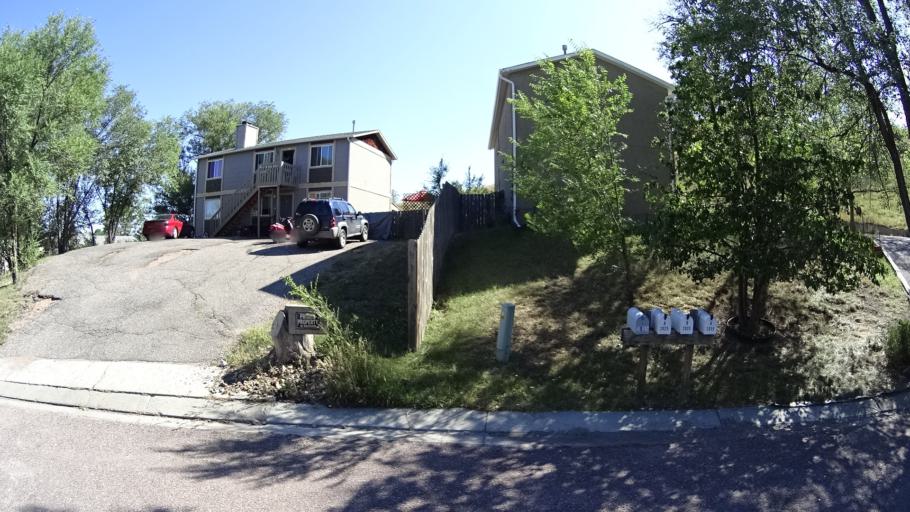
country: US
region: Colorado
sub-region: El Paso County
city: Colorado Springs
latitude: 38.8528
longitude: -104.8518
